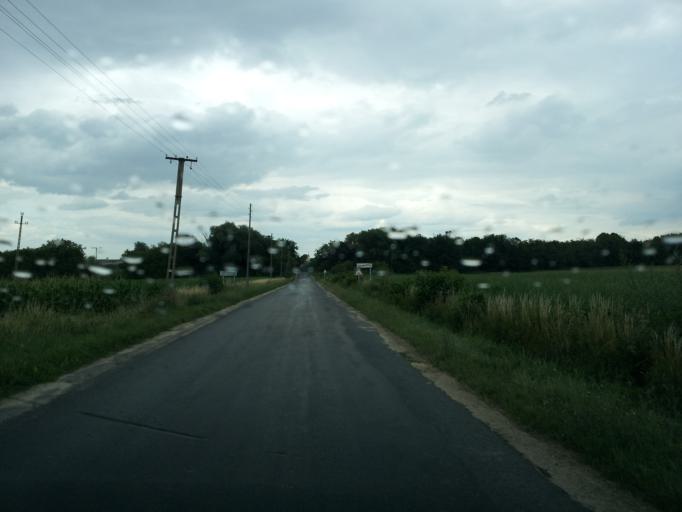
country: HU
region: Zala
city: Turje
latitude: 47.0857
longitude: 17.0292
